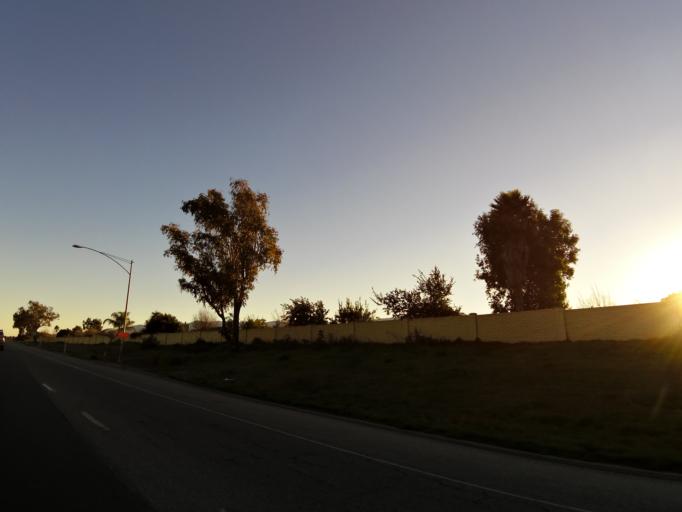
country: US
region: California
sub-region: Monterey County
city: Gonzales
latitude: 36.5112
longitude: -121.4368
